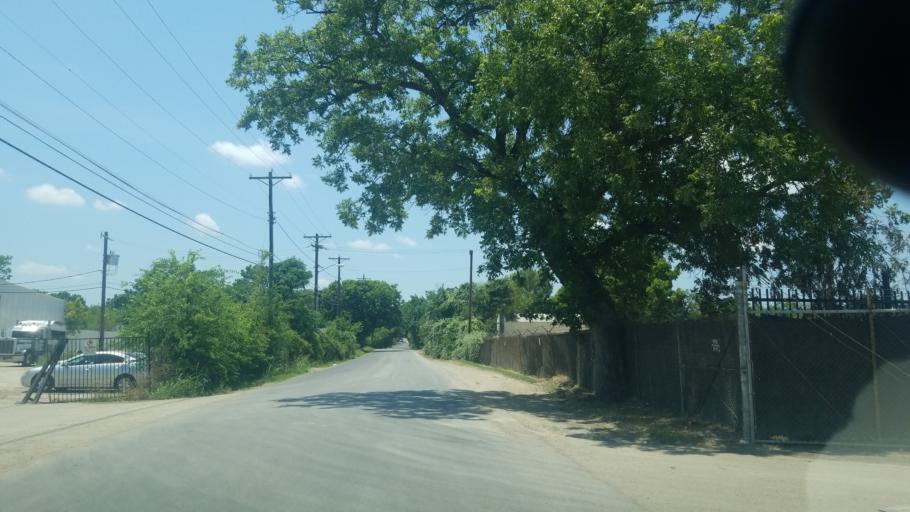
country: US
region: Texas
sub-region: Dallas County
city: Dallas
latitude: 32.7443
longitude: -96.7822
